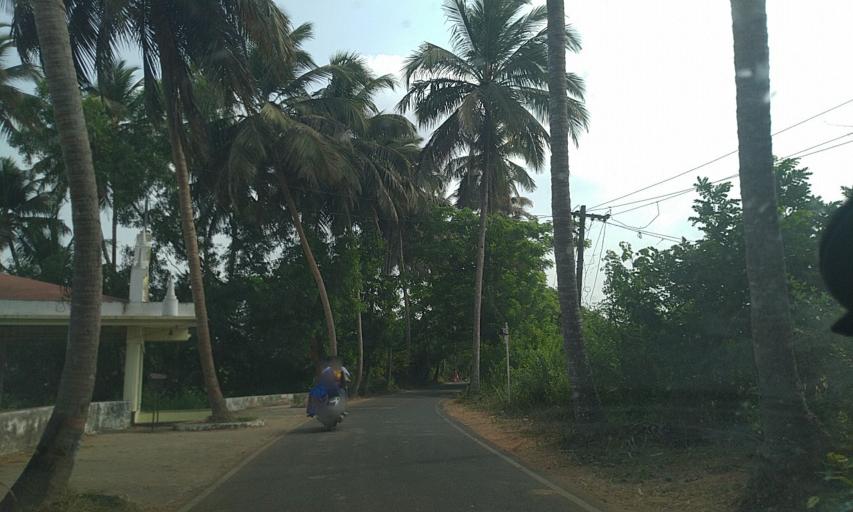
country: IN
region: Goa
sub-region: North Goa
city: Taleigao
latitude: 15.4727
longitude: 73.8413
